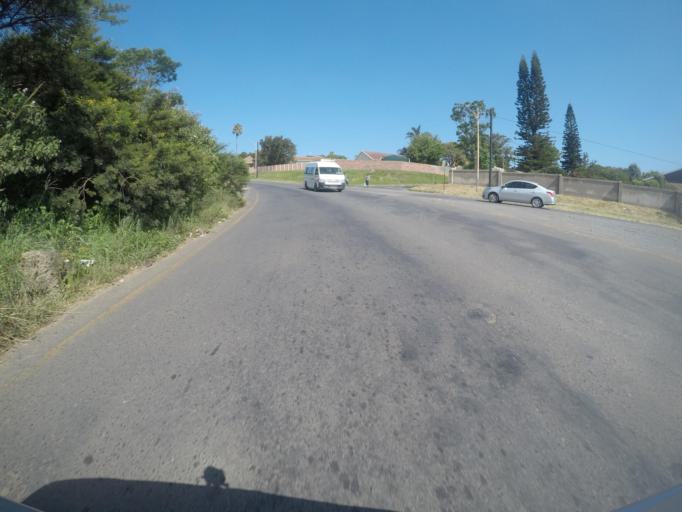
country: ZA
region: Eastern Cape
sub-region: Buffalo City Metropolitan Municipality
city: East London
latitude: -32.9716
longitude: 27.8793
